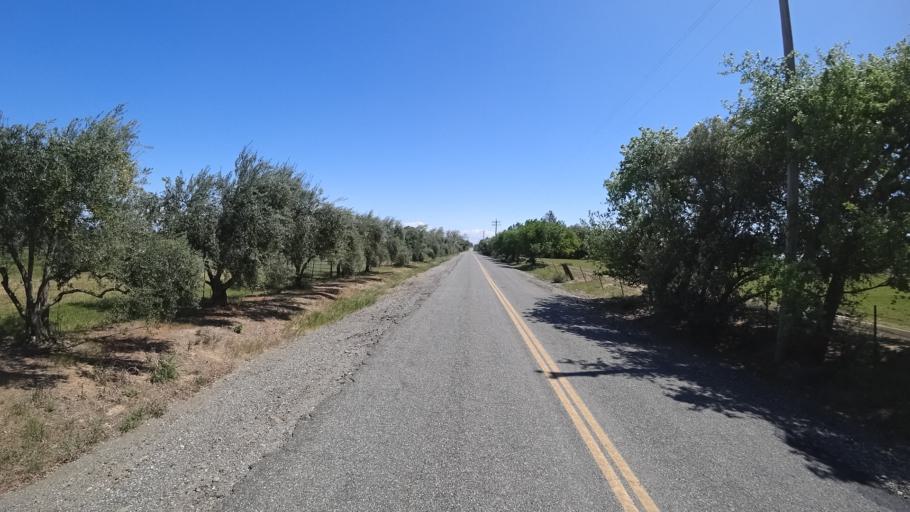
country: US
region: California
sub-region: Glenn County
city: Orland
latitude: 39.7839
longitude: -122.2146
